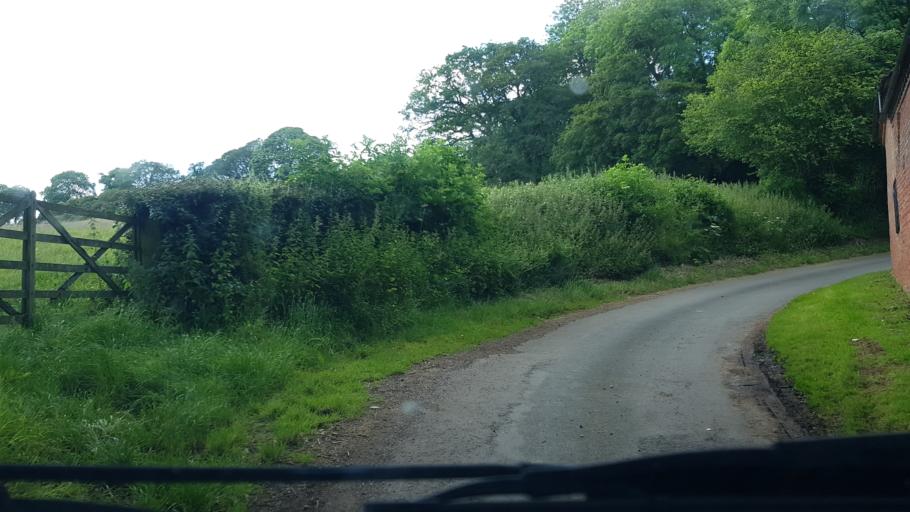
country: GB
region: England
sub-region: Shropshire
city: Romsley
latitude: 52.4628
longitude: -2.2656
